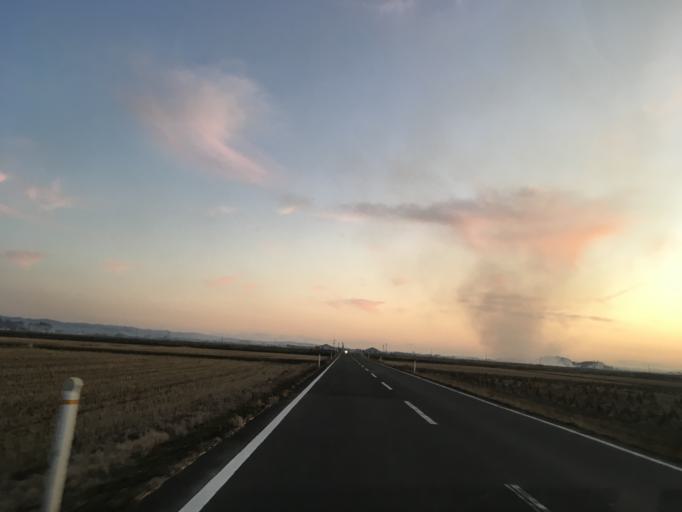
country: JP
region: Iwate
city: Ichinoseki
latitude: 38.7507
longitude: 141.2368
